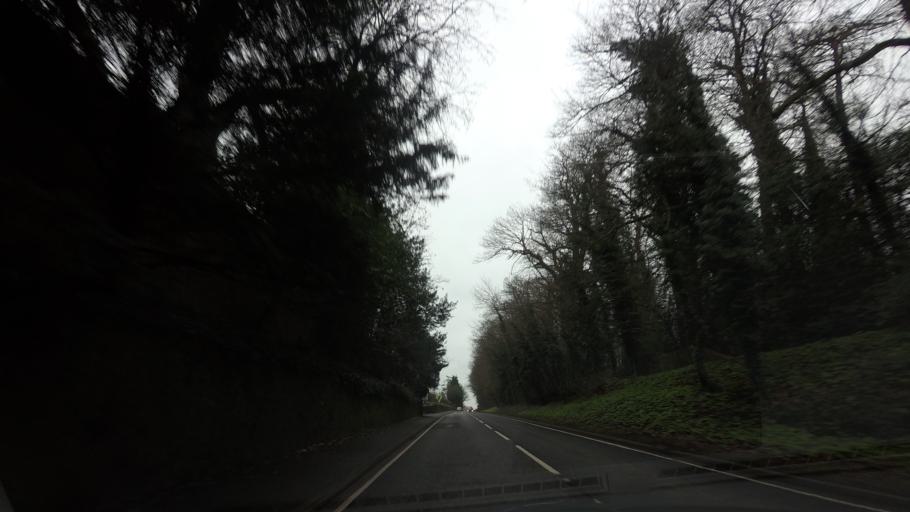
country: GB
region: England
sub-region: Kent
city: Maidstone
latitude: 51.2265
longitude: 0.5112
